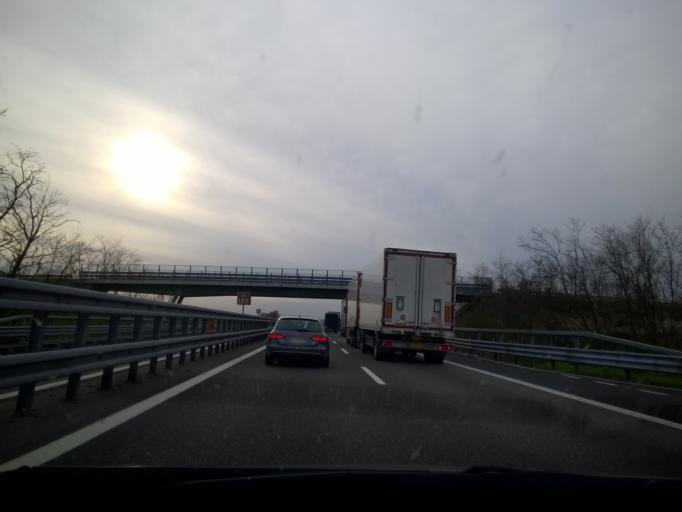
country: IT
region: Emilia-Romagna
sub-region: Provincia di Piacenza
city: Sarmato
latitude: 45.0679
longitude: 9.5150
